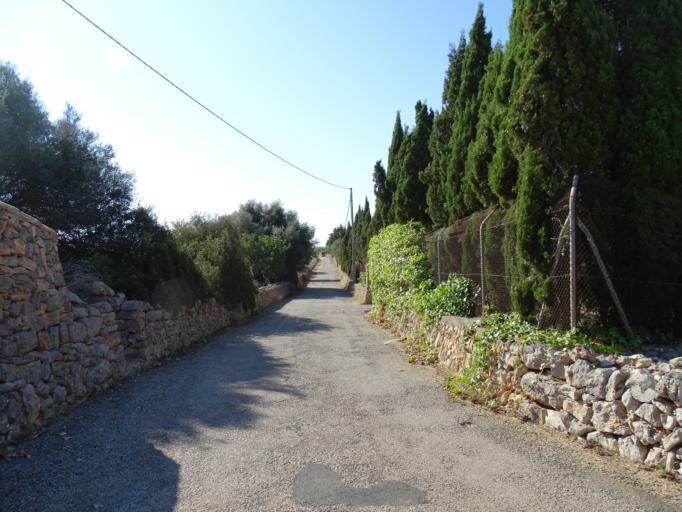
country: ES
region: Balearic Islands
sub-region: Illes Balears
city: Santanyi
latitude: 39.3960
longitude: 3.2179
